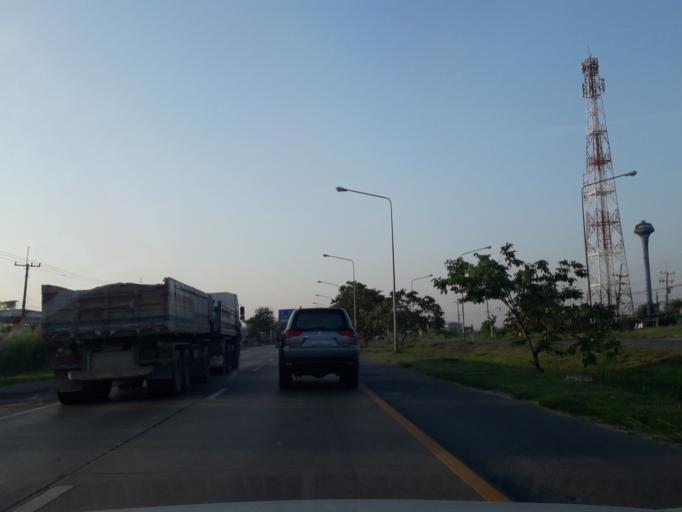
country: TH
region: Phra Nakhon Si Ayutthaya
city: Phra Nakhon Si Ayutthaya
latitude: 14.3458
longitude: 100.5283
